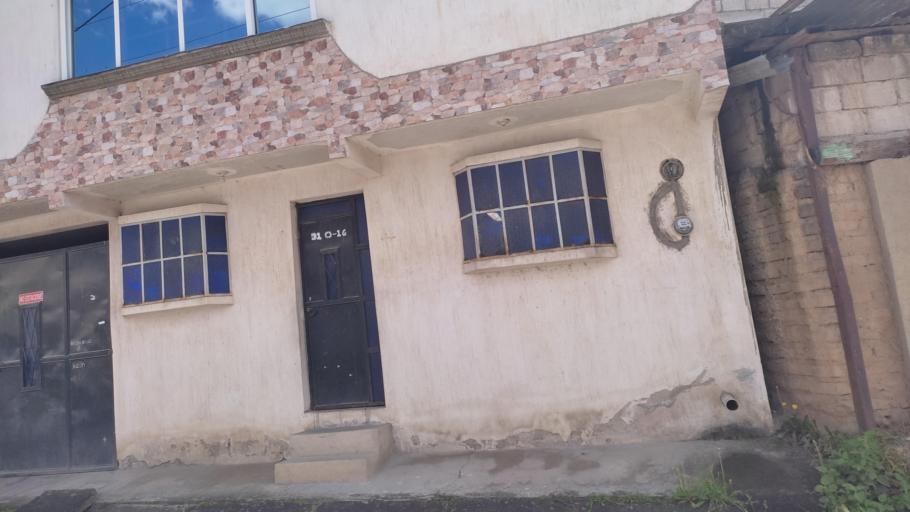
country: GT
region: Quetzaltenango
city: Quetzaltenango
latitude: 14.8555
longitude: -91.5256
